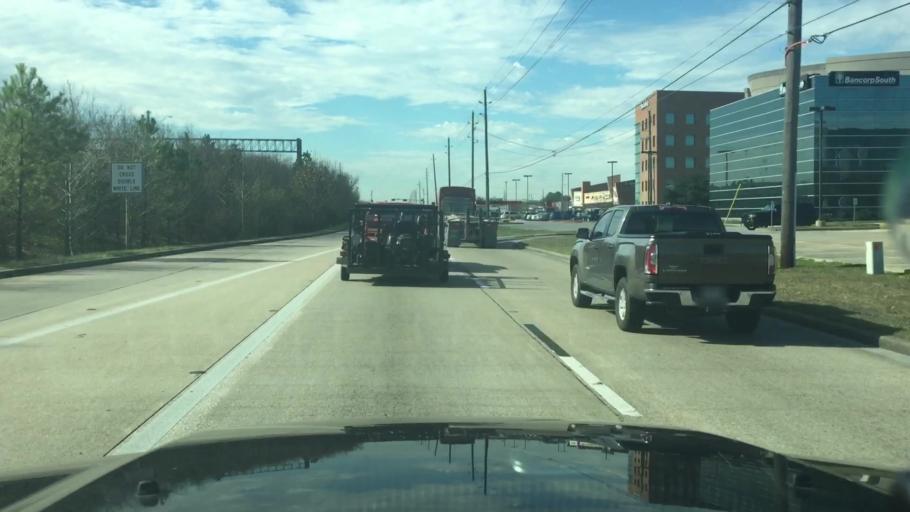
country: US
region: Texas
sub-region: Harris County
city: Jersey Village
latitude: 29.9313
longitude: -95.5417
